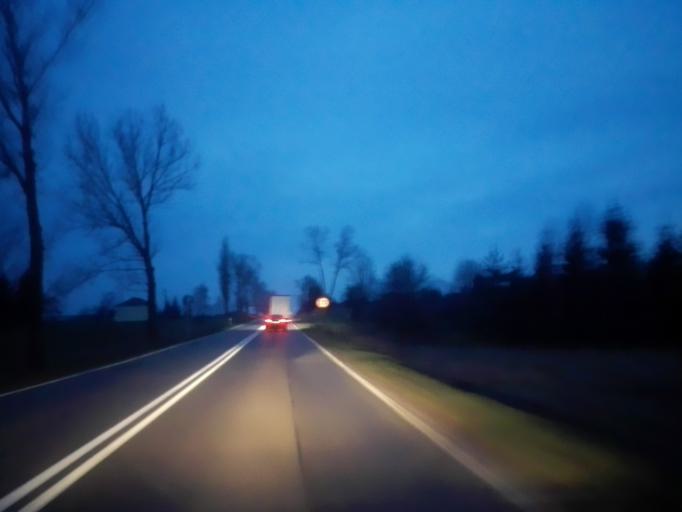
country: PL
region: Podlasie
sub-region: Lomza
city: Lomza
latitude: 53.1104
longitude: 22.0292
